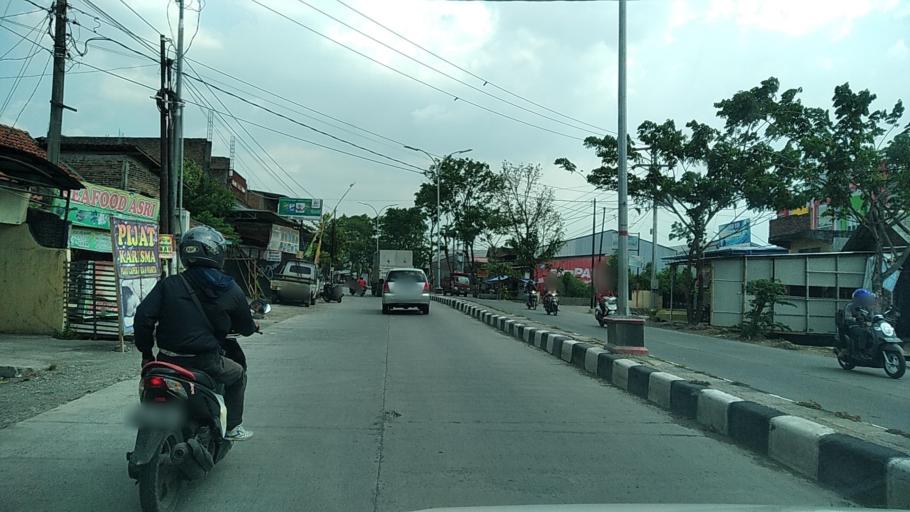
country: ID
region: Central Java
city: Semarang
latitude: -6.9629
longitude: 110.4787
